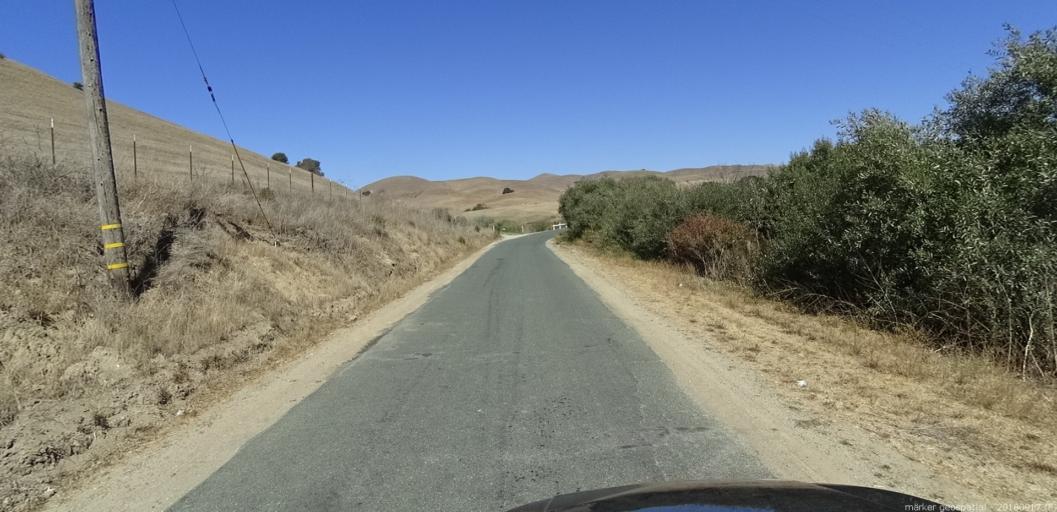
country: US
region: California
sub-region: San Benito County
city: San Juan Bautista
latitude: 36.7884
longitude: -121.5894
